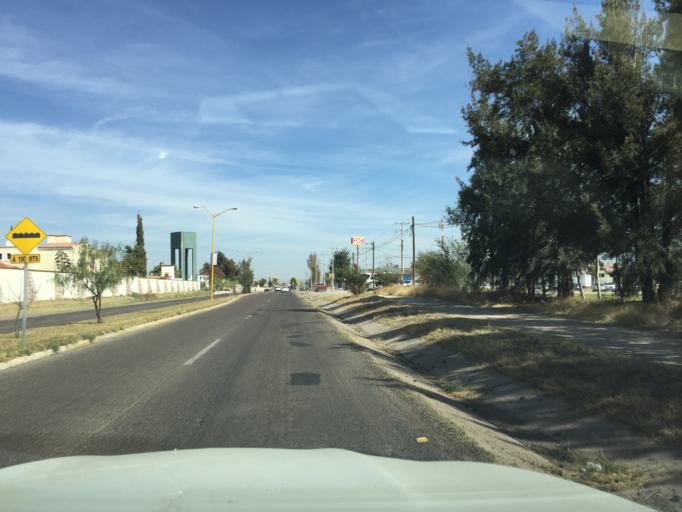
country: MX
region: Aguascalientes
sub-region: Aguascalientes
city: La Loma de los Negritos
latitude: 21.8574
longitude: -102.3472
